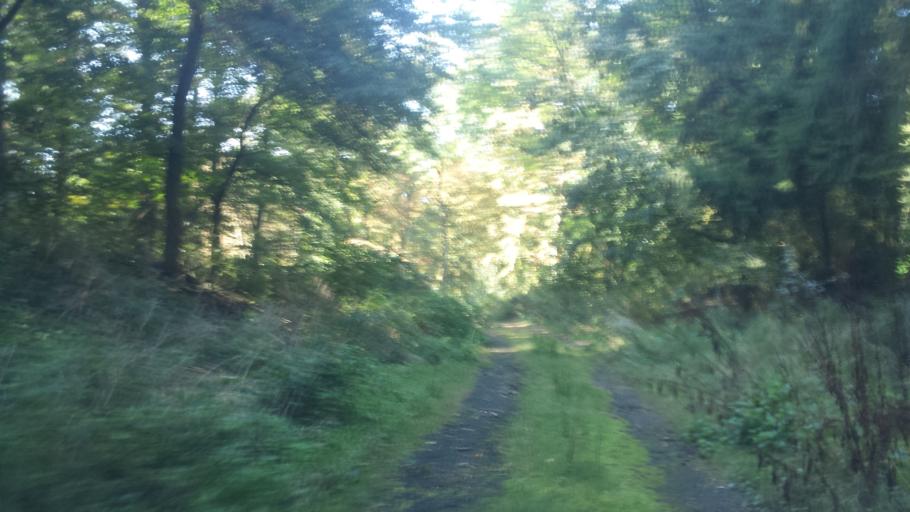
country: DE
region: Rheinland-Pfalz
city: Gollheim
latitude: 49.5759
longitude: 8.0273
